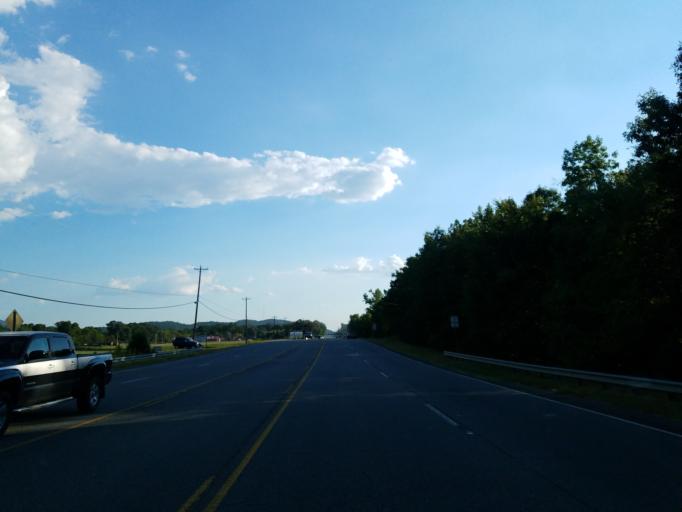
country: US
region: Georgia
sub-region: Murray County
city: Chatsworth
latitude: 34.8468
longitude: -84.7560
